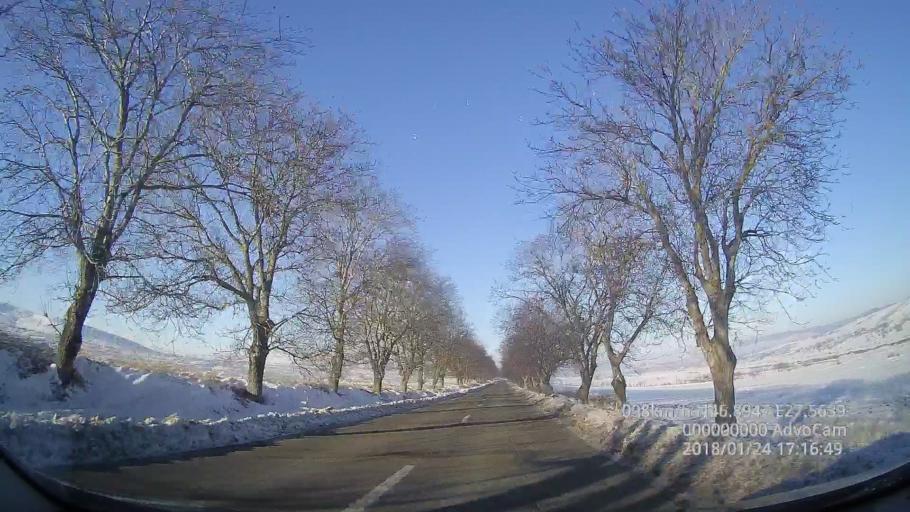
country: RO
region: Iasi
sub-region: Comuna Scanteia
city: Scanteia
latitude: 46.8954
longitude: 27.5638
